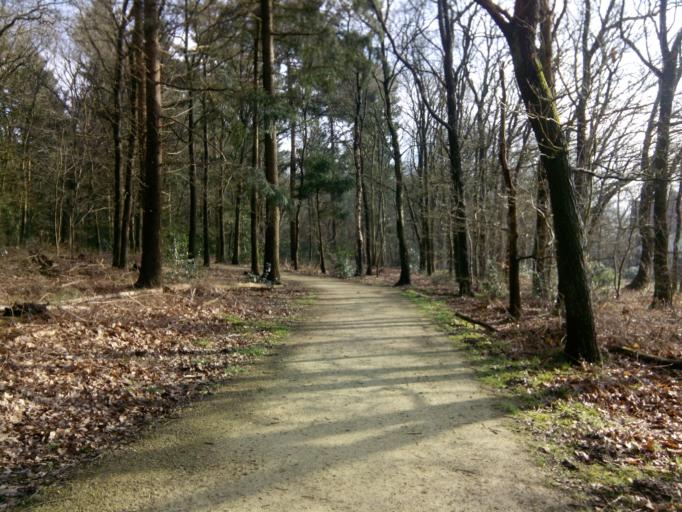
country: NL
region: Utrecht
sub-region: Gemeente Utrechtse Heuvelrug
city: Amerongen
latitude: 52.0092
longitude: 5.4564
